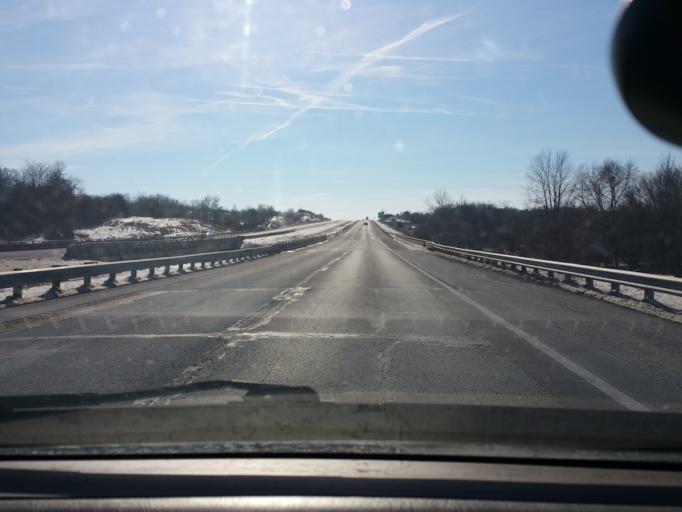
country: US
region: Missouri
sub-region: Harrison County
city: Bethany
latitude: 40.2331
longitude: -94.0130
